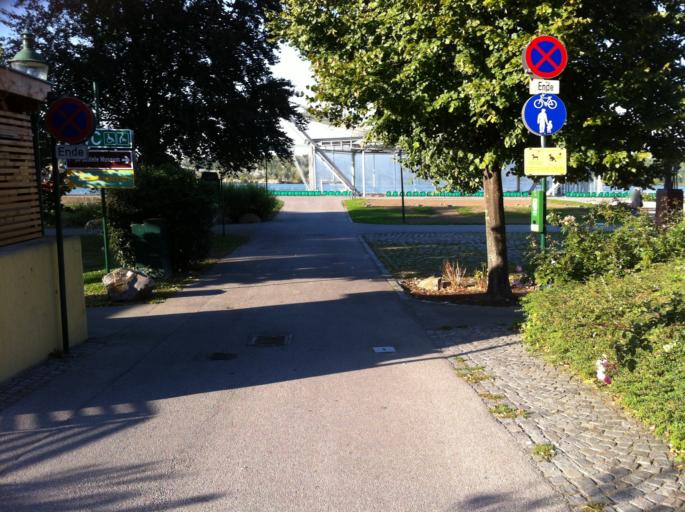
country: AT
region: Lower Austria
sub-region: Politischer Bezirk Tulln
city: Tulln
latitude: 48.3332
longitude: 16.0527
